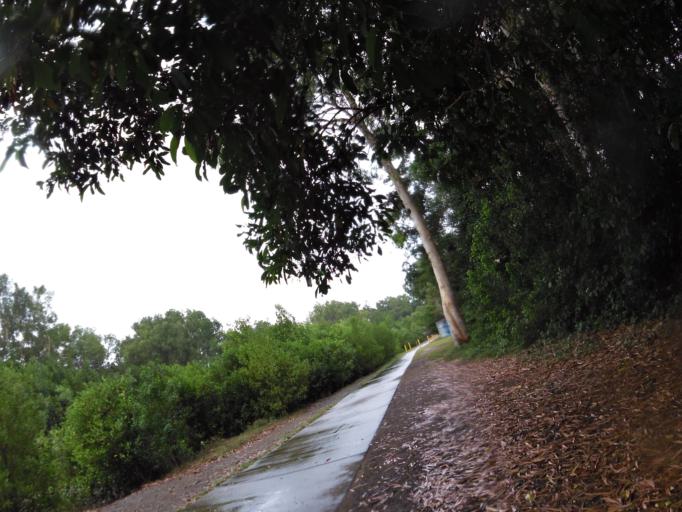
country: AU
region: Queensland
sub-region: Cairns
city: Cairns
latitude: -16.8983
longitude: 145.7539
